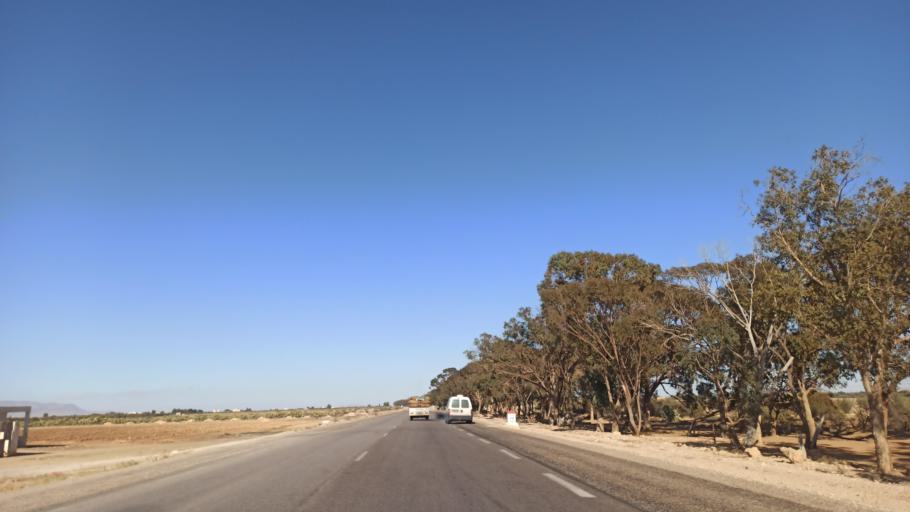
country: TN
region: Sidi Bu Zayd
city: Jilma
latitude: 35.2005
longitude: 9.3776
